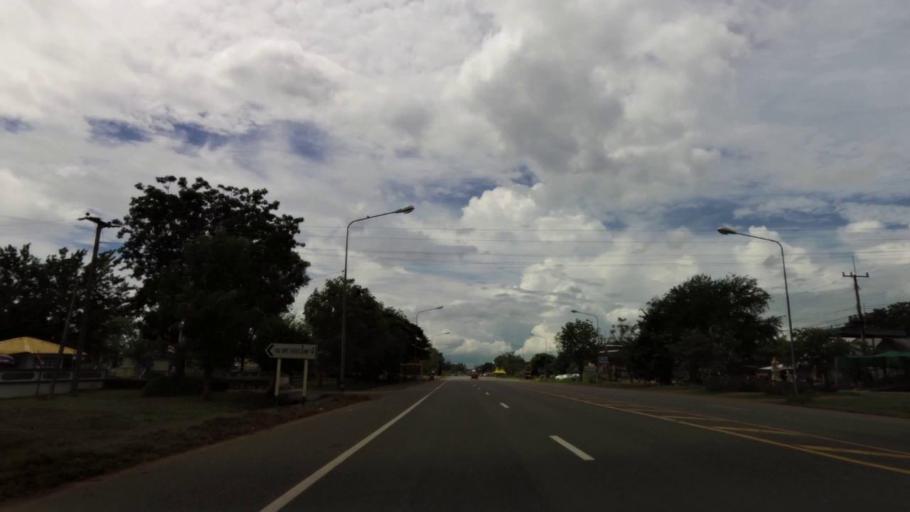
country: TH
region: Nakhon Sawan
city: Phai Sali
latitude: 15.5993
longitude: 100.6621
